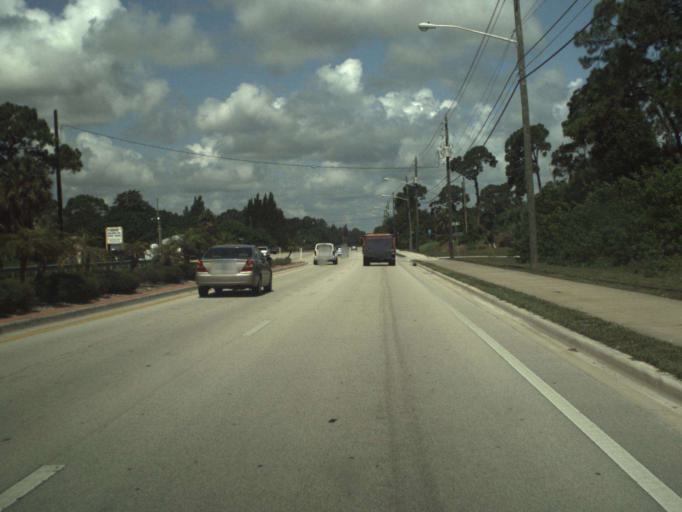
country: US
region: Florida
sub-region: Indian River County
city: Florida Ridge
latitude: 27.5870
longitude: -80.3928
